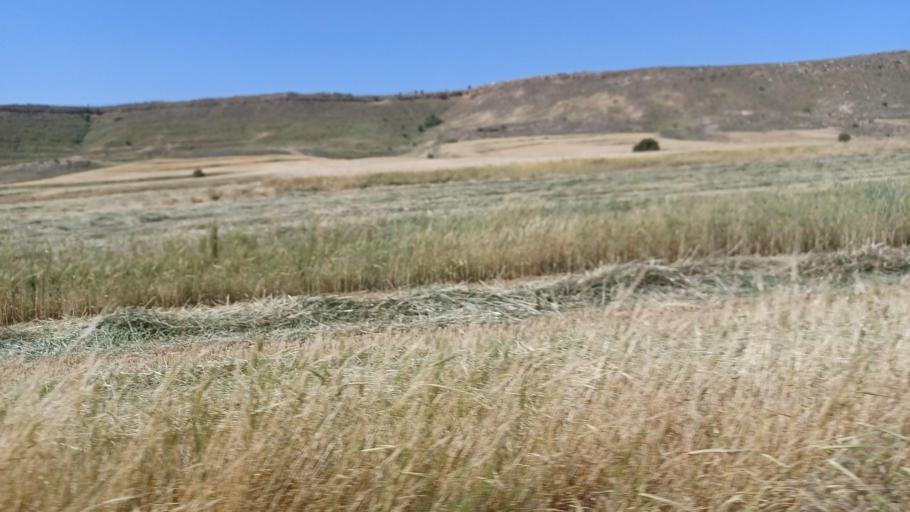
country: CY
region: Lefkosia
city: Mammari
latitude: 35.1734
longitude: 33.2218
